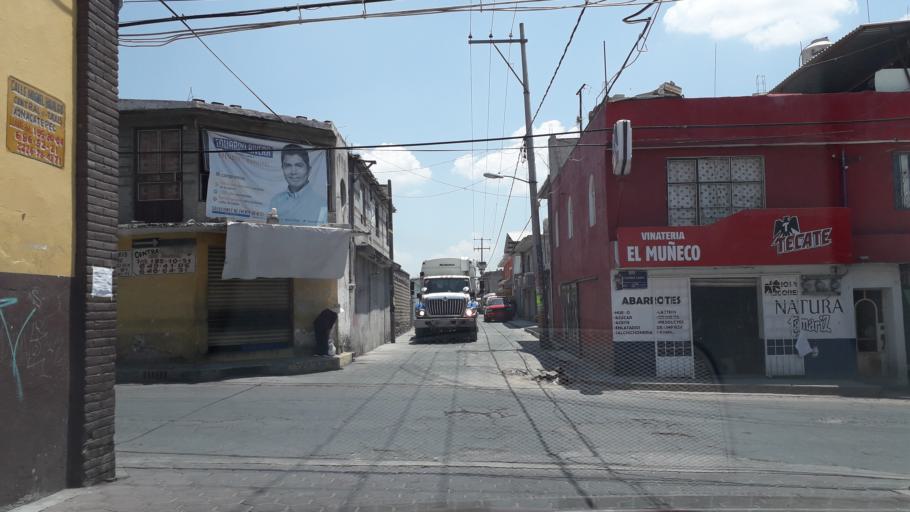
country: MX
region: Puebla
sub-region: Puebla
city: Santa Maria Xonacatepec
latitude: 19.0872
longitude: -98.1042
